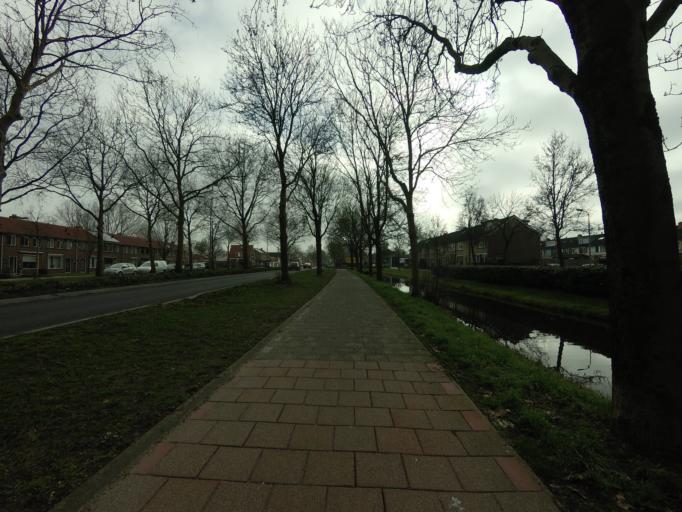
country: NL
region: Utrecht
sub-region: Gemeente Oudewater
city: Oudewater
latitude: 52.0285
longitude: 4.8652
